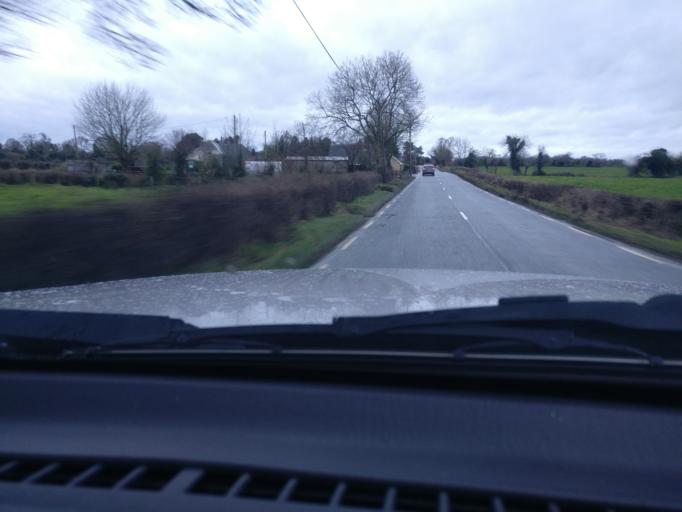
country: IE
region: Leinster
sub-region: An Mhi
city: Longwood
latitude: 53.4983
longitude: -6.8573
